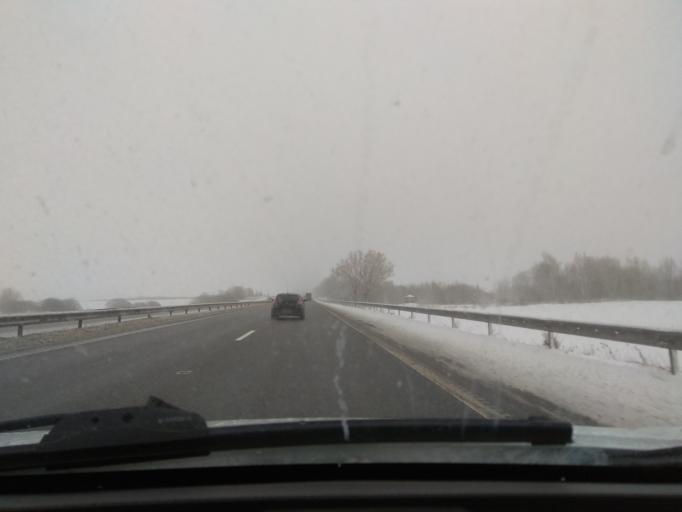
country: LT
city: Kaisiadorys
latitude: 54.8667
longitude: 24.2495
